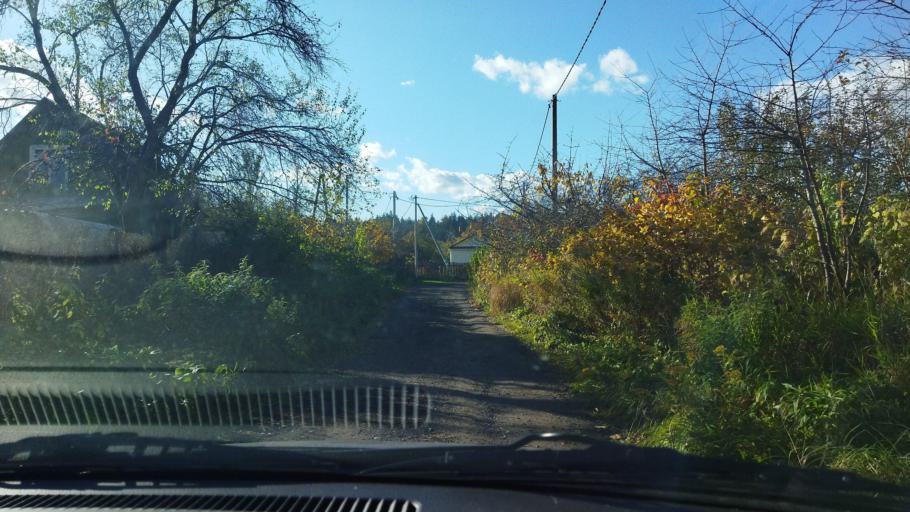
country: BY
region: Minsk
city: Slabada
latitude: 53.9883
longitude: 27.8943
